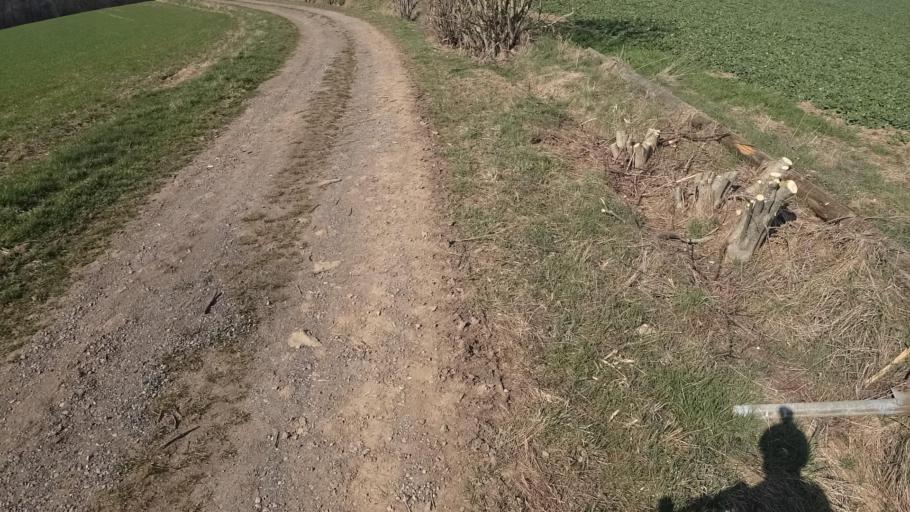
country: DE
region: Rheinland-Pfalz
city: Rheinbollen
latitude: 50.0177
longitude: 7.6627
